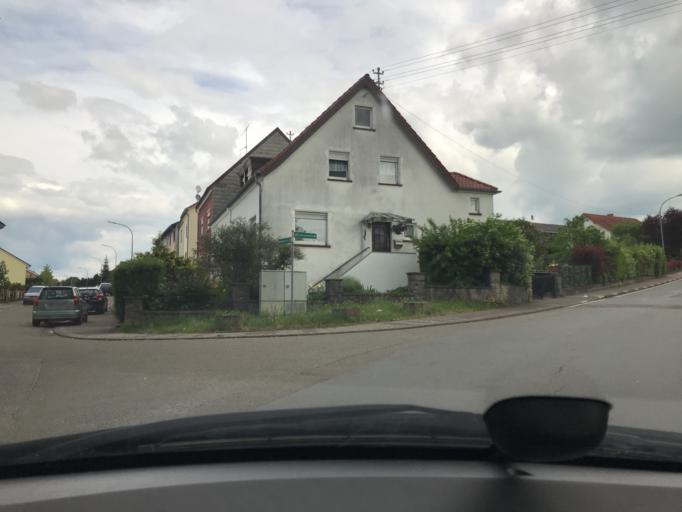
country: DE
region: Saarland
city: Kleinblittersdorf
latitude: 49.1628
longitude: 7.0393
